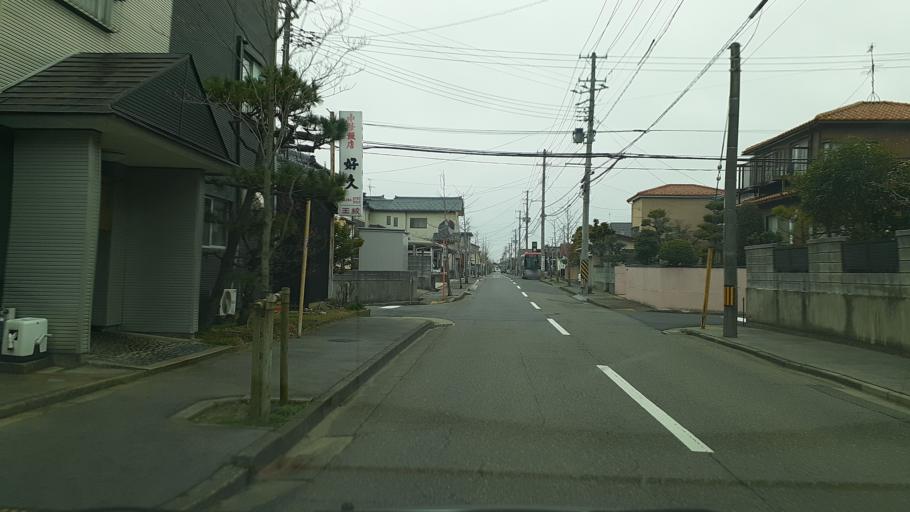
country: JP
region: Niigata
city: Niigata-shi
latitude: 37.8640
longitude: 139.0411
